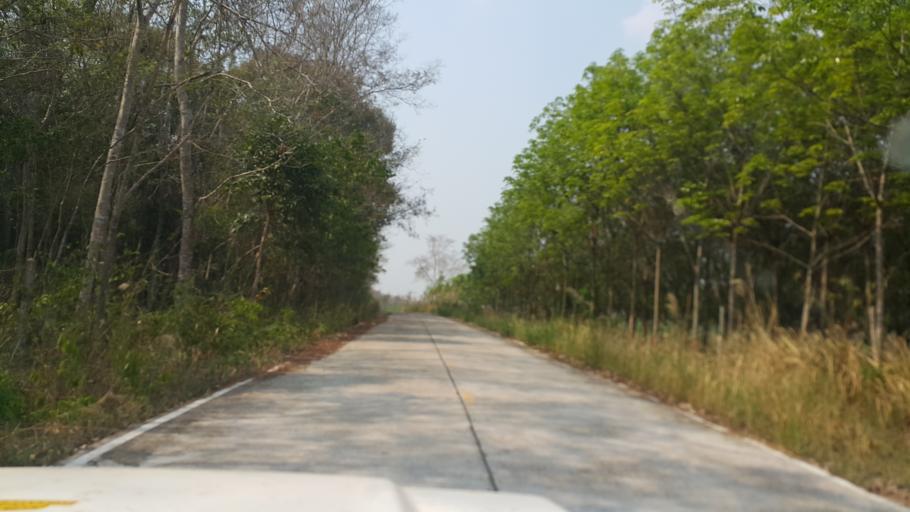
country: TH
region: Nakhon Phanom
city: Ban Phaeng
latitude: 17.9747
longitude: 104.1504
